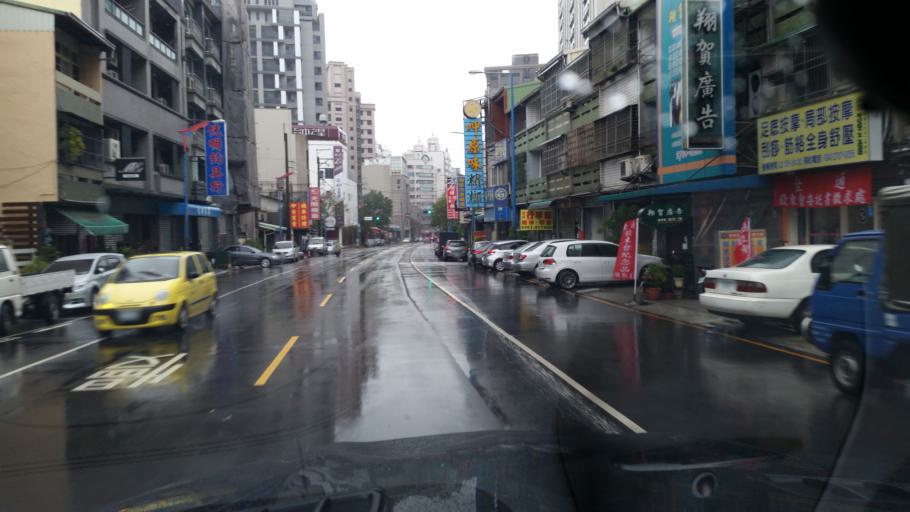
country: TW
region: Taiwan
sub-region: Taichung City
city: Taichung
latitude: 24.1848
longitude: 120.6398
